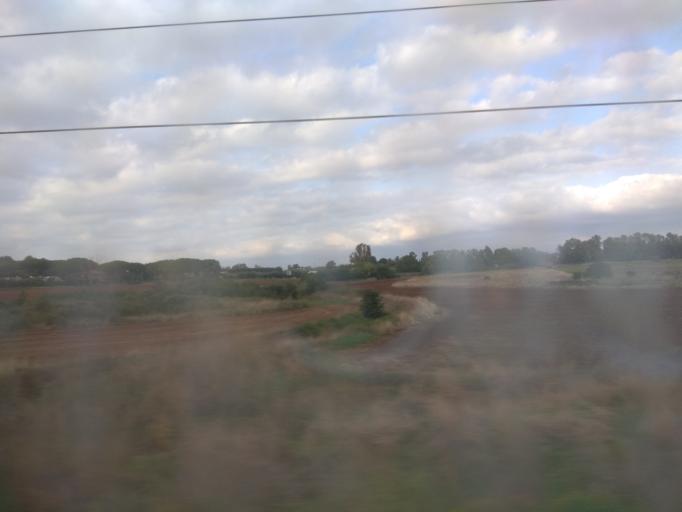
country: IT
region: Latium
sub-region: Citta metropolitana di Roma Capitale
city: Marina San Nicola
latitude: 41.9327
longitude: 12.1379
